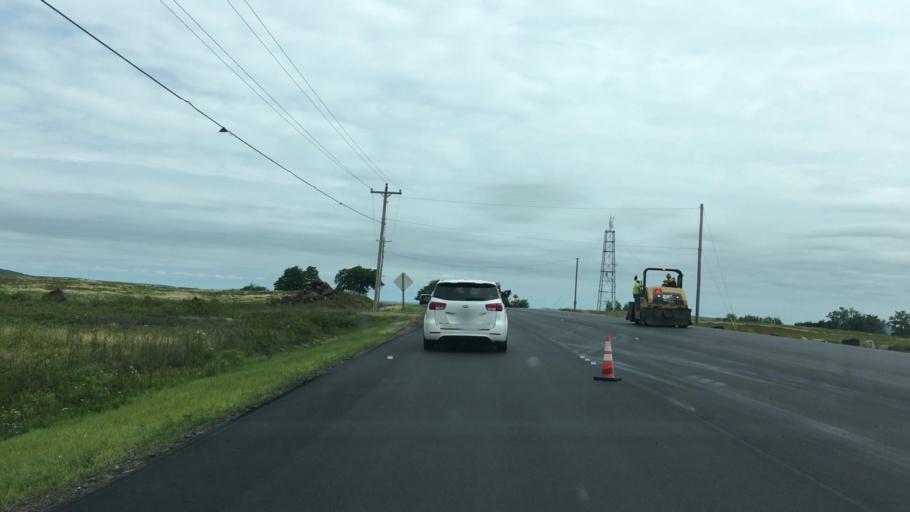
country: US
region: Maine
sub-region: Washington County
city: Machias
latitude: 44.9663
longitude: -67.6494
